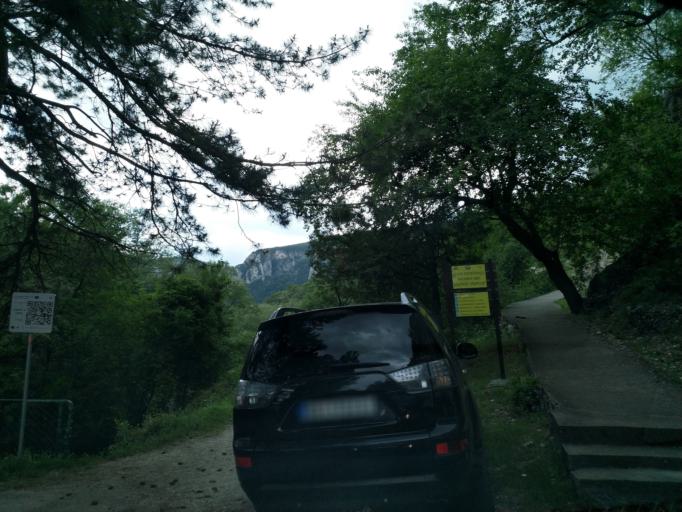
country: RS
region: Central Serbia
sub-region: Borski Okrug
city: Bor
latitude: 44.0294
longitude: 21.9623
